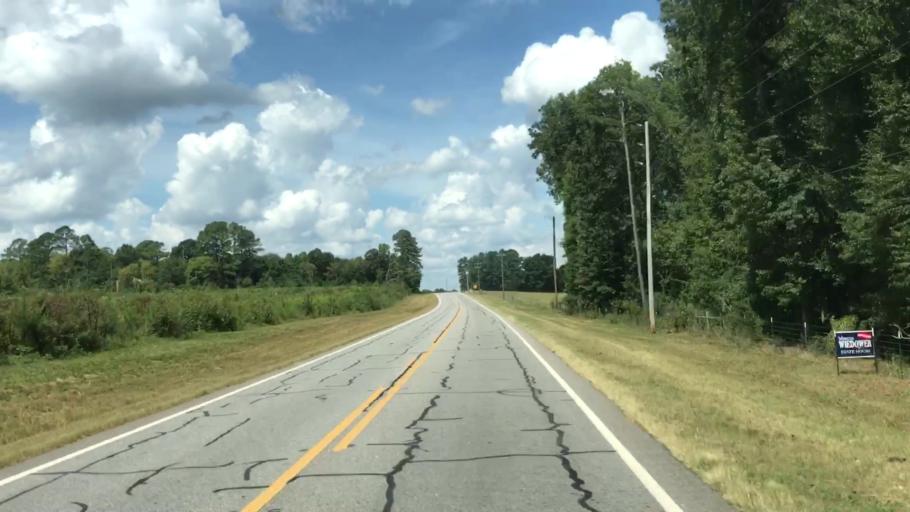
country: US
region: Georgia
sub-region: Oconee County
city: Watkinsville
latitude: 33.7888
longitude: -83.3193
